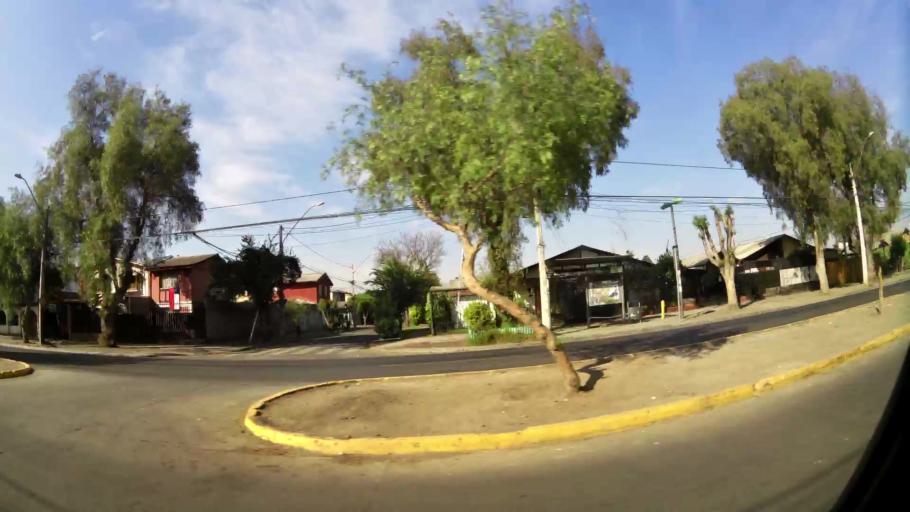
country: CL
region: Santiago Metropolitan
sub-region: Provincia de Santiago
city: Lo Prado
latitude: -33.4576
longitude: -70.7419
